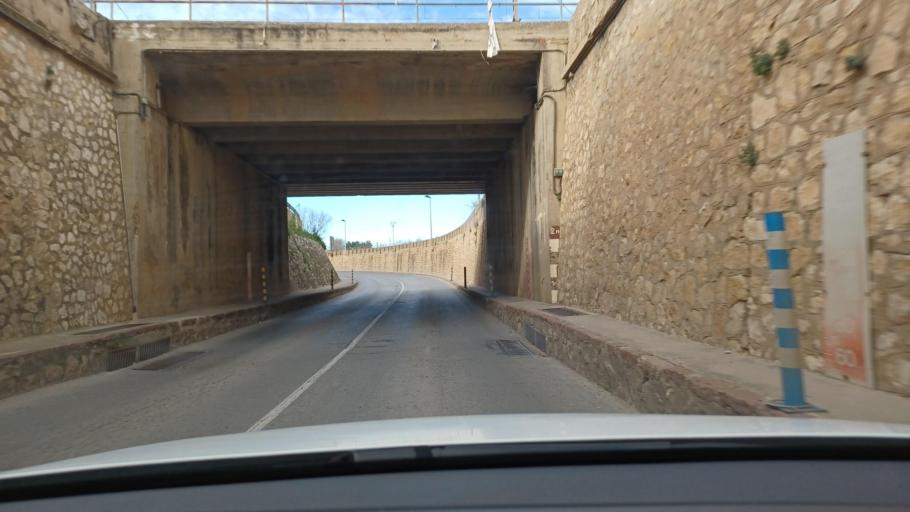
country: ES
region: Valencia
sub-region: Provincia de Valencia
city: Benifaio
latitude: 39.2888
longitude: -0.4297
